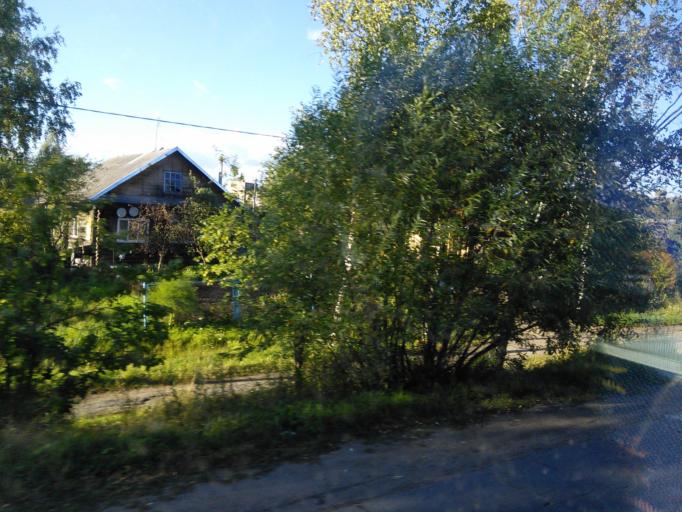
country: RU
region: Jaroslavl
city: Poshekhon'ye
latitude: 58.4982
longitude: 39.1056
